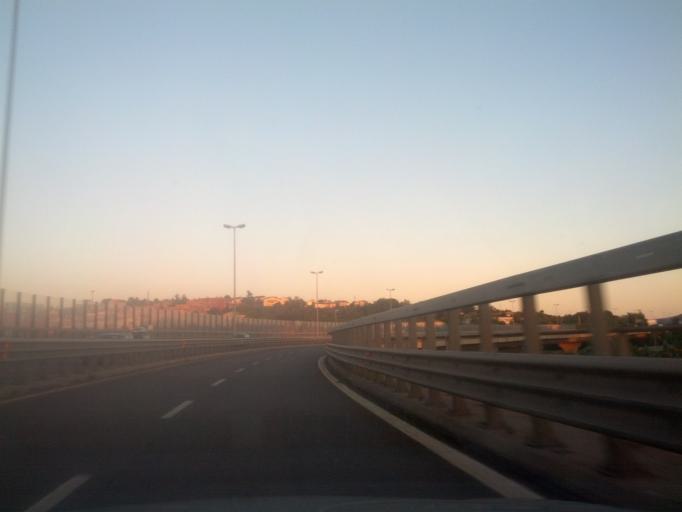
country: IT
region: Friuli Venezia Giulia
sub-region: Provincia di Trieste
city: Muggia
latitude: 45.6201
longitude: 13.7839
